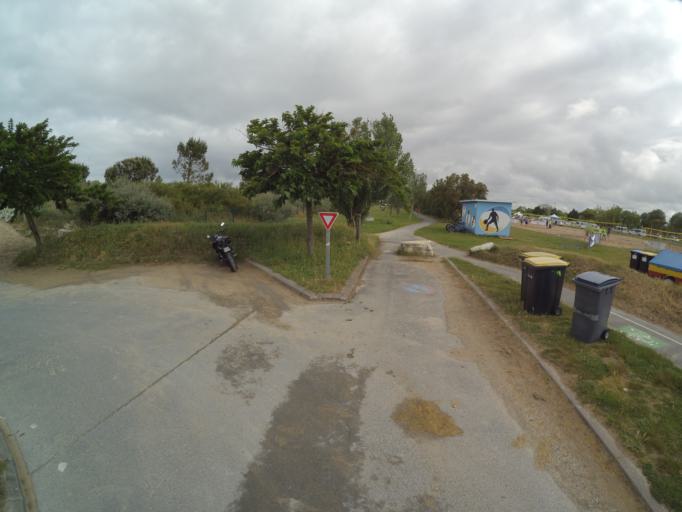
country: FR
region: Poitou-Charentes
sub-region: Departement de la Charente-Maritime
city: Angoulins
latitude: 46.1160
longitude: -1.1233
